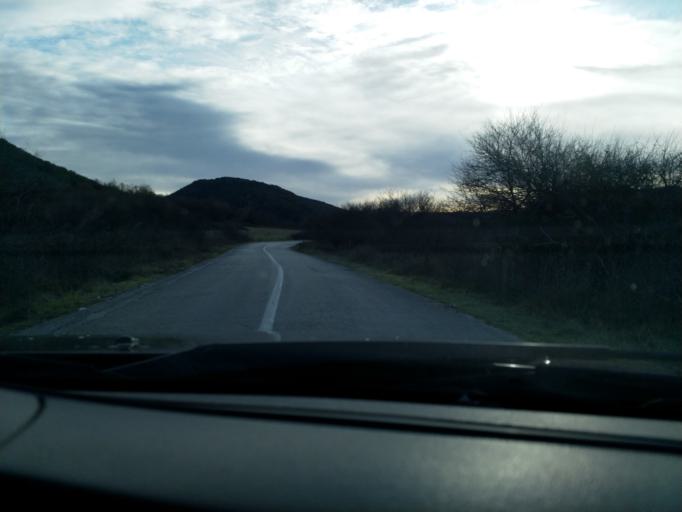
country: GR
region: Epirus
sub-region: Nomos Ioanninon
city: Asprangeloi
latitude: 39.8693
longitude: 20.7109
